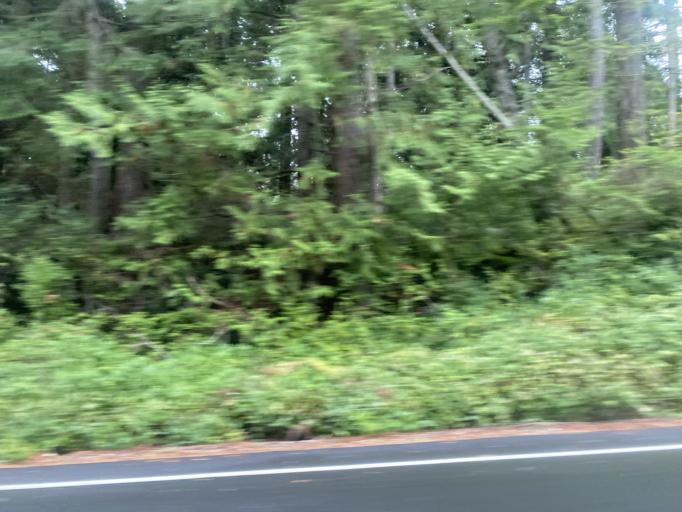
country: US
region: Washington
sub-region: Island County
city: Freeland
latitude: 48.0728
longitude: -122.4851
